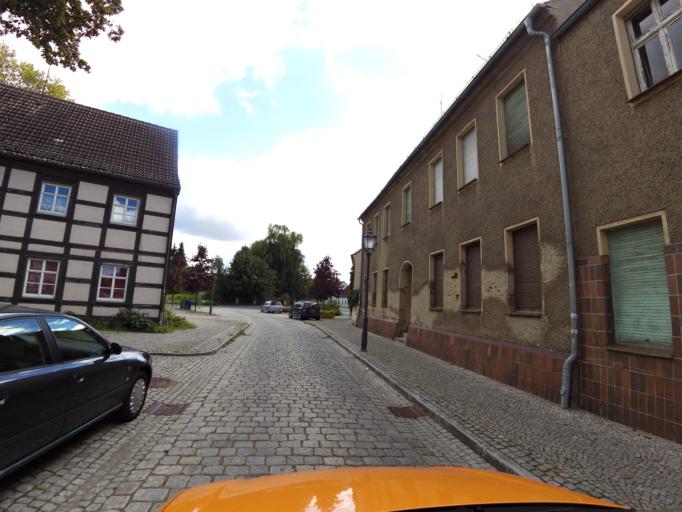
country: DE
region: Brandenburg
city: Luckenwalde
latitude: 52.0885
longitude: 13.1775
